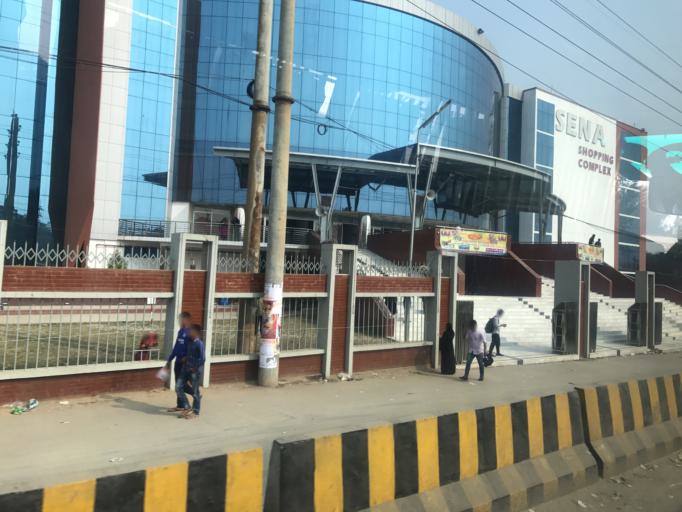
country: BD
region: Dhaka
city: Tungi
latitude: 23.9126
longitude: 90.2596
